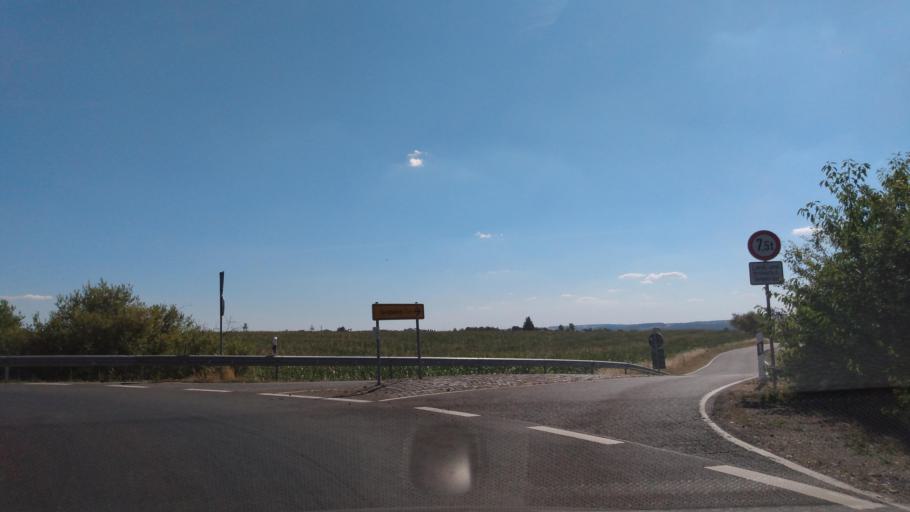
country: DE
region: Rheinland-Pfalz
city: Spangdahlem
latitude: 49.9948
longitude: 6.6967
